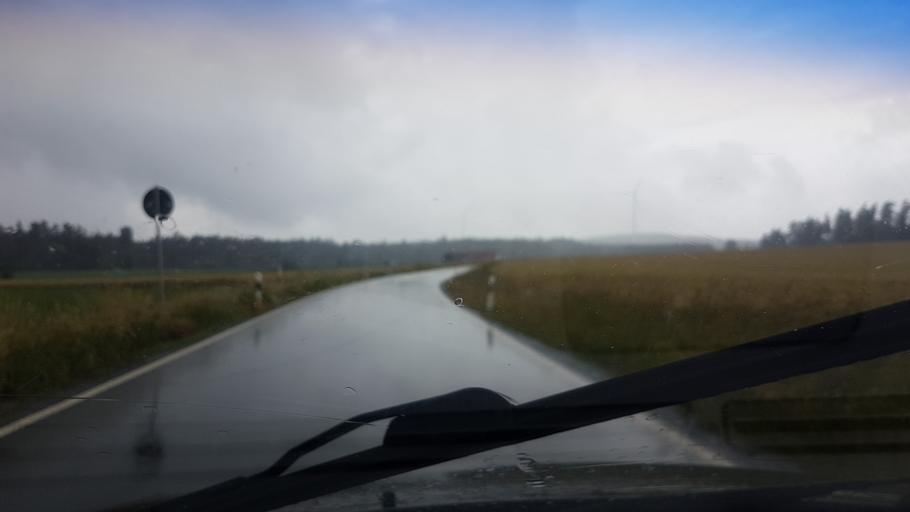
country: DE
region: Bavaria
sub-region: Upper Franconia
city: Schirnding
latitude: 50.0453
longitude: 12.2413
